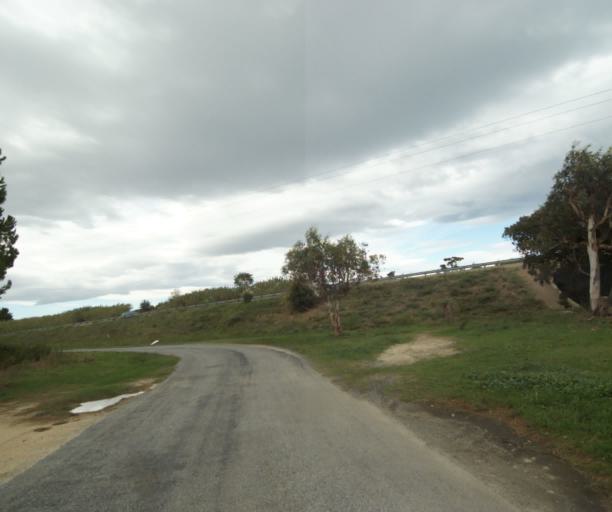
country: FR
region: Languedoc-Roussillon
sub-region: Departement des Pyrenees-Orientales
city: Argelers
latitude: 42.5391
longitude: 3.0220
